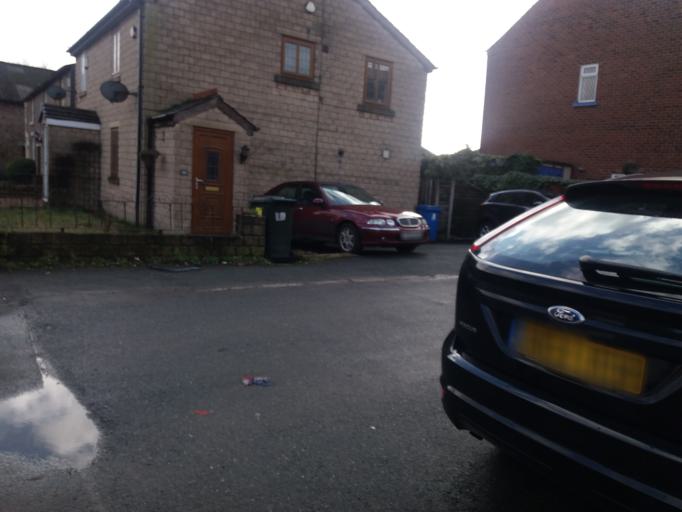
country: GB
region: England
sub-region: Lancashire
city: Adlington
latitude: 53.6098
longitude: -2.6049
